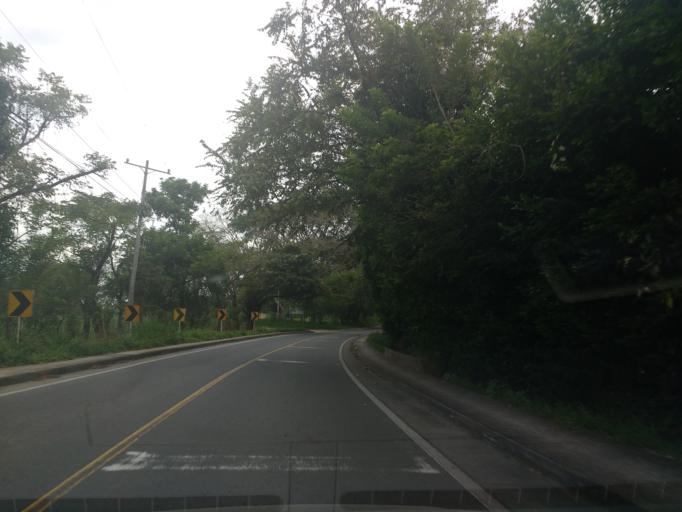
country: CO
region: Cauca
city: Miranda
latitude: 3.2796
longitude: -76.2224
